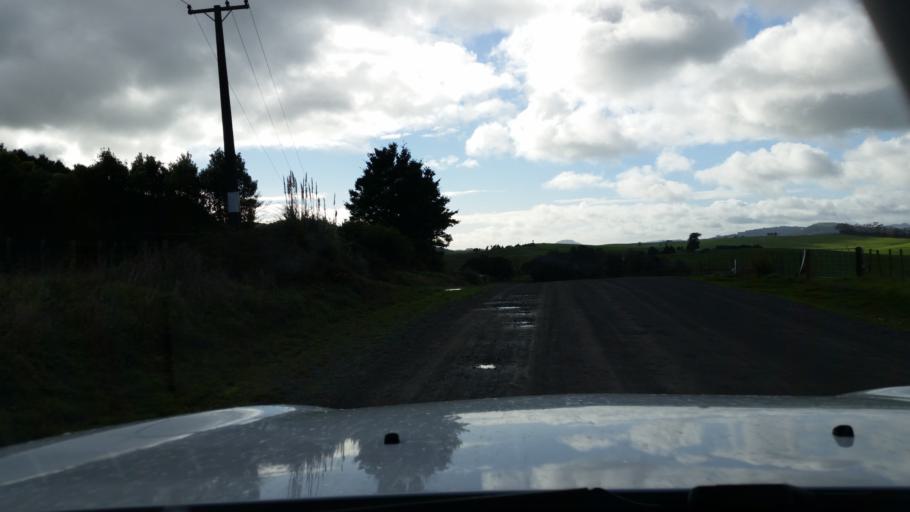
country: NZ
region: Northland
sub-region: Whangarei
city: Maungatapere
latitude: -35.6662
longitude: 174.1021
